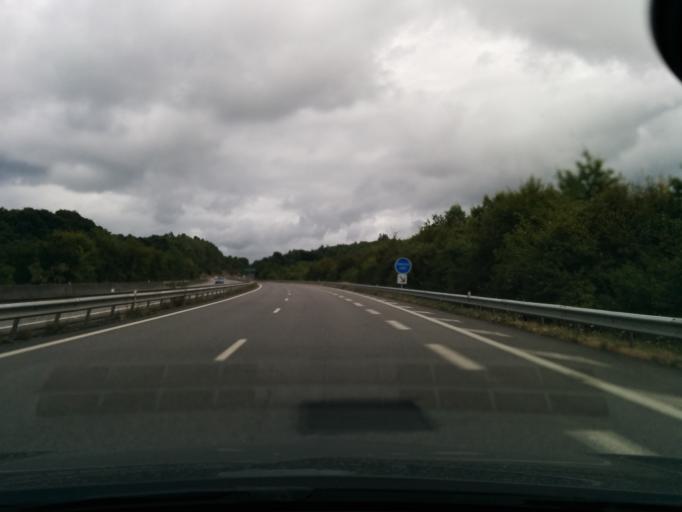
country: FR
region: Limousin
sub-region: Departement de la Haute-Vienne
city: Razes
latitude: 46.0446
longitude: 1.3541
